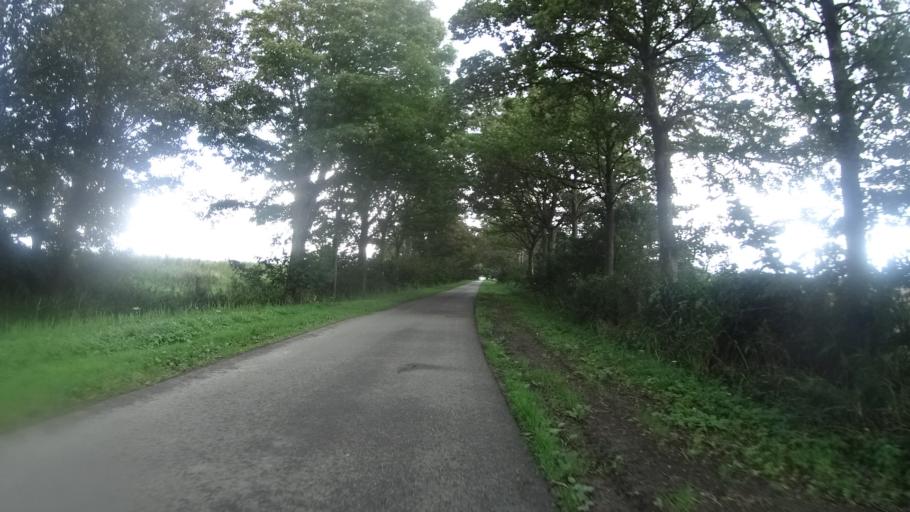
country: NL
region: North Holland
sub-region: Gemeente Hollands Kroon
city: Den Oever
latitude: 52.8974
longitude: 4.9900
